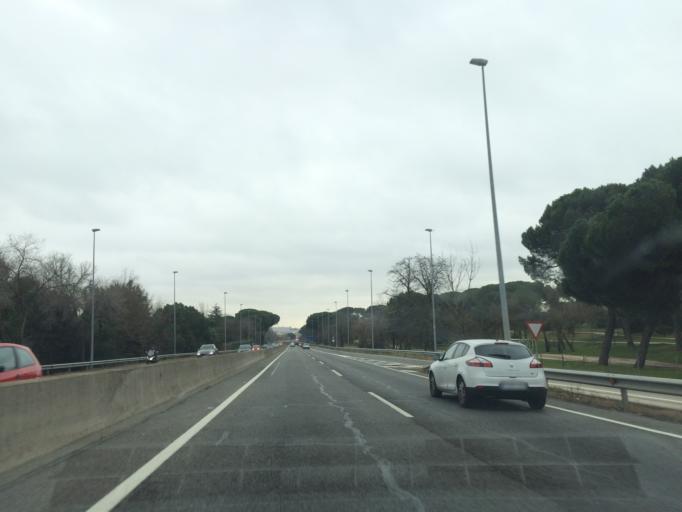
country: ES
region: Madrid
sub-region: Provincia de Madrid
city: Moncloa-Aravaca
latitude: 40.4427
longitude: -3.7483
